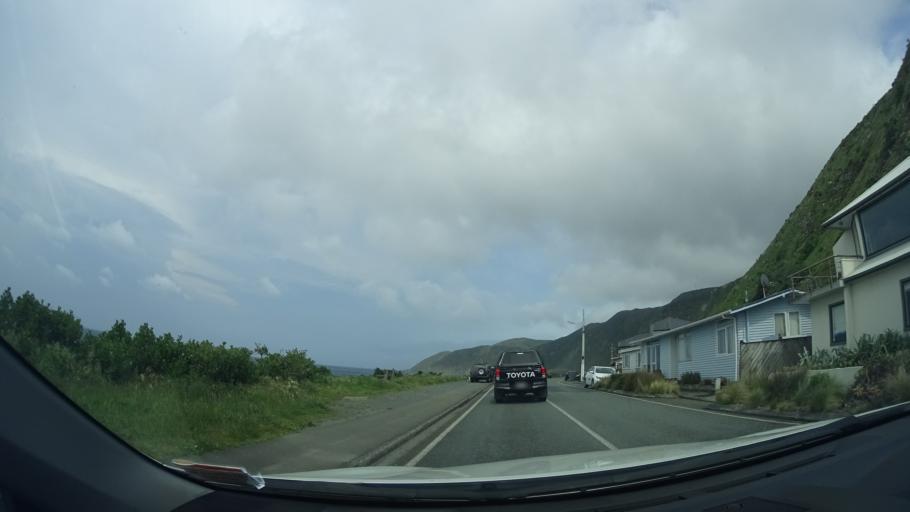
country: NZ
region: Wellington
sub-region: Wellington City
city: Brooklyn
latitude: -41.3488
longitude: 174.7519
